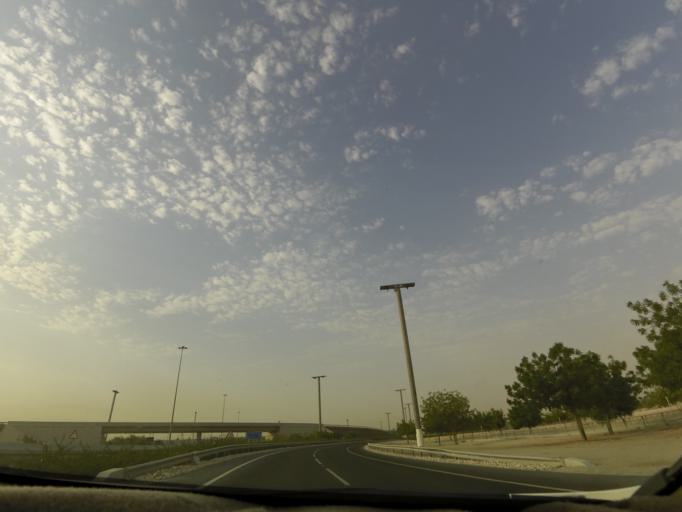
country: QA
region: Al Wakrah
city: Al Wakrah
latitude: 25.2433
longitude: 51.5896
